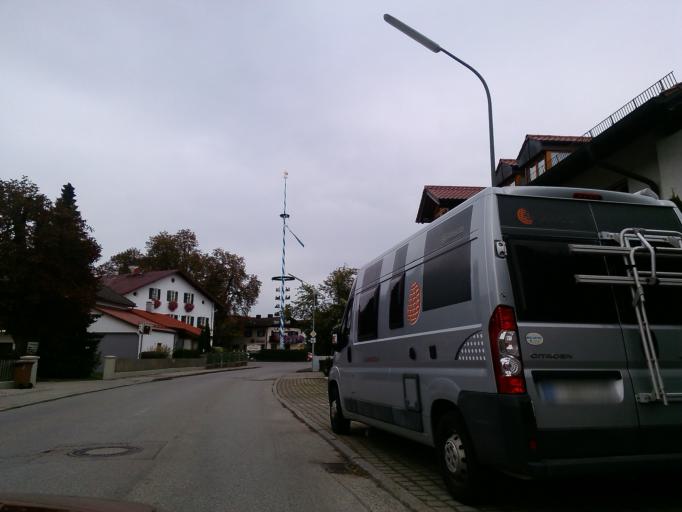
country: DE
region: Bavaria
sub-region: Upper Bavaria
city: Gauting
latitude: 48.0653
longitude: 11.3250
